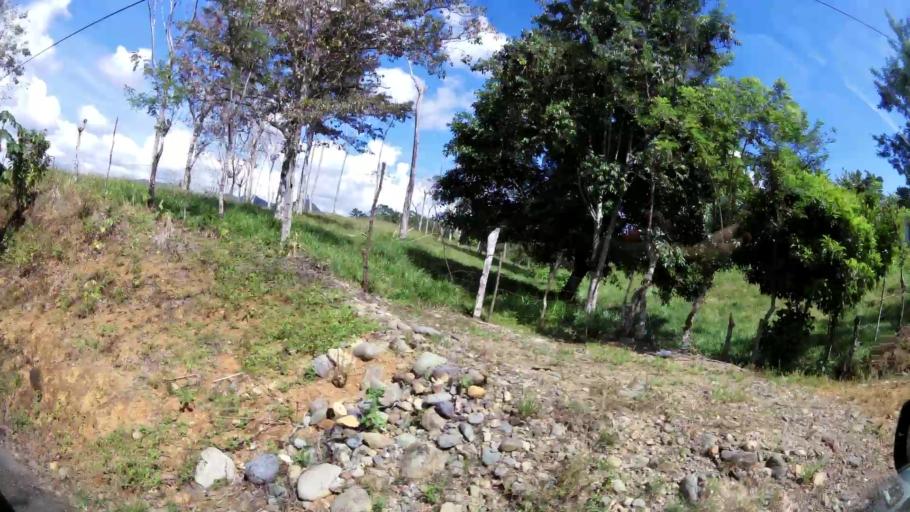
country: CR
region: San Jose
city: San Isidro
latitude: 9.3863
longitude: -83.6987
